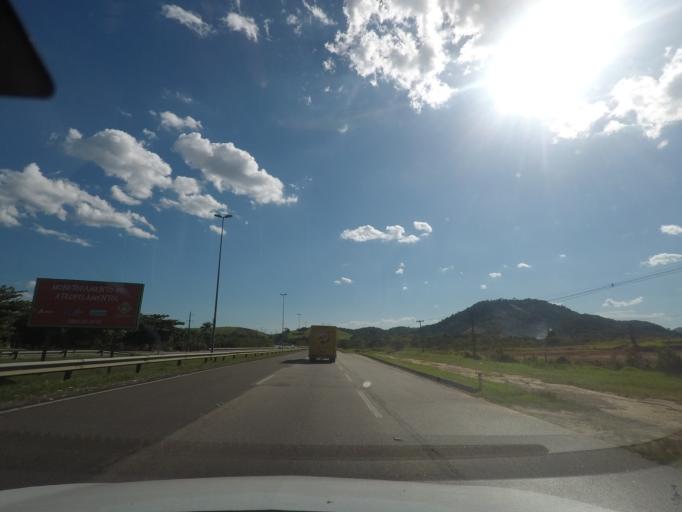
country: BR
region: Rio de Janeiro
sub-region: Guapimirim
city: Guapimirim
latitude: -22.5845
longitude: -43.0160
